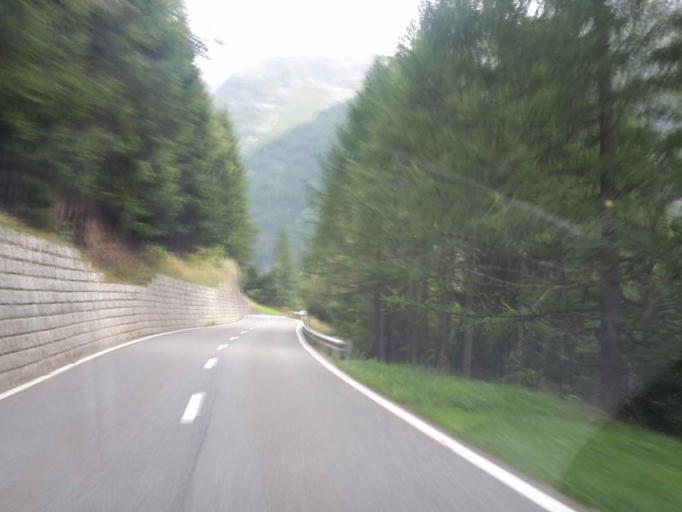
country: CH
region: Valais
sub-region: Martigny District
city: Martigny-Combe
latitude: 46.0469
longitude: 6.9973
